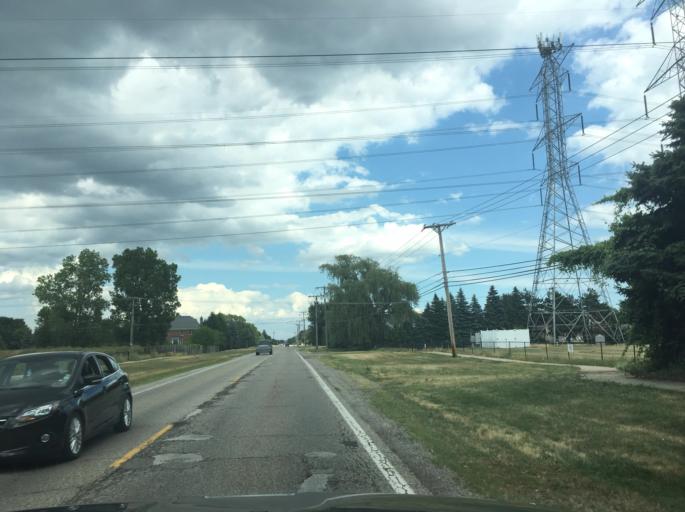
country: US
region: Michigan
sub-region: Macomb County
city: Utica
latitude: 42.6410
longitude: -83.0038
